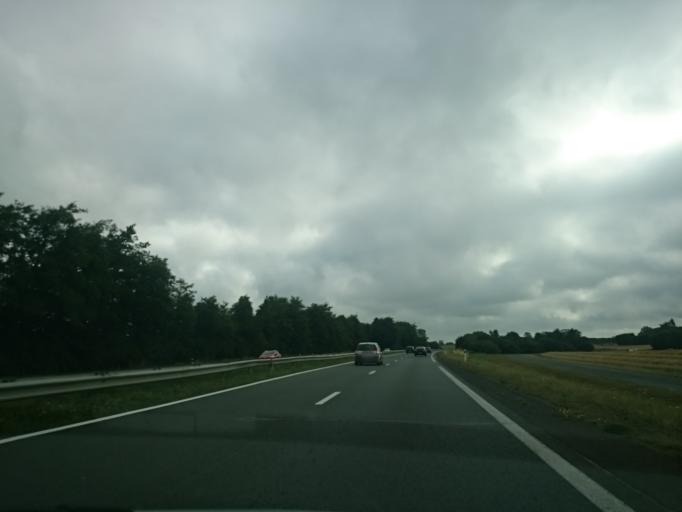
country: FR
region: Brittany
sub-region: Departement des Cotes-d'Armor
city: Tremuson
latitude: 48.5412
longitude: -2.8385
